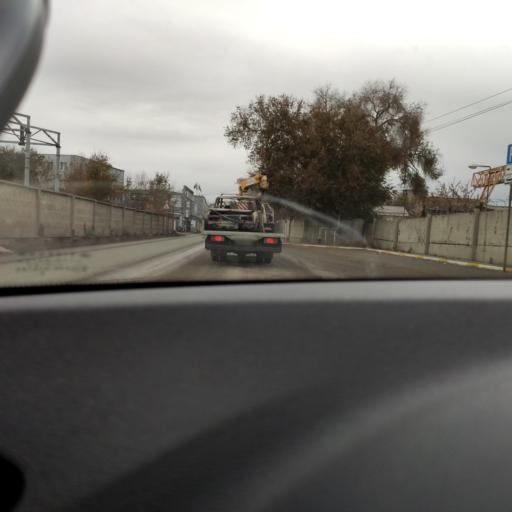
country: RU
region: Samara
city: Smyshlyayevka
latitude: 53.2081
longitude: 50.3019
